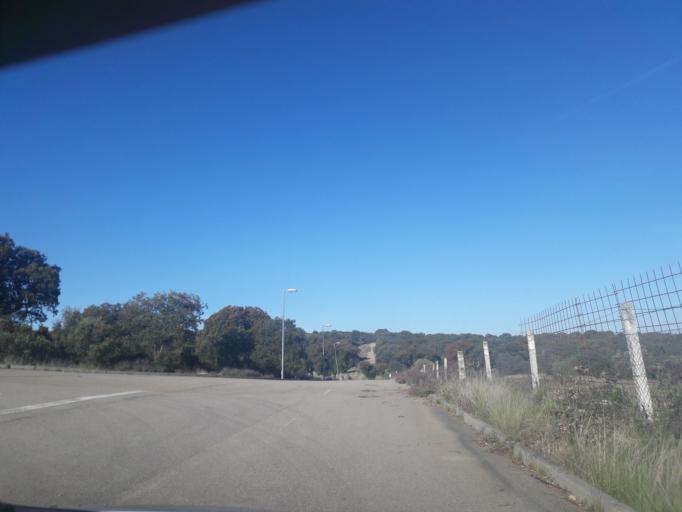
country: ES
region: Castille and Leon
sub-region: Provincia de Salamanca
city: Martinamor
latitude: 40.8119
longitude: -5.6430
